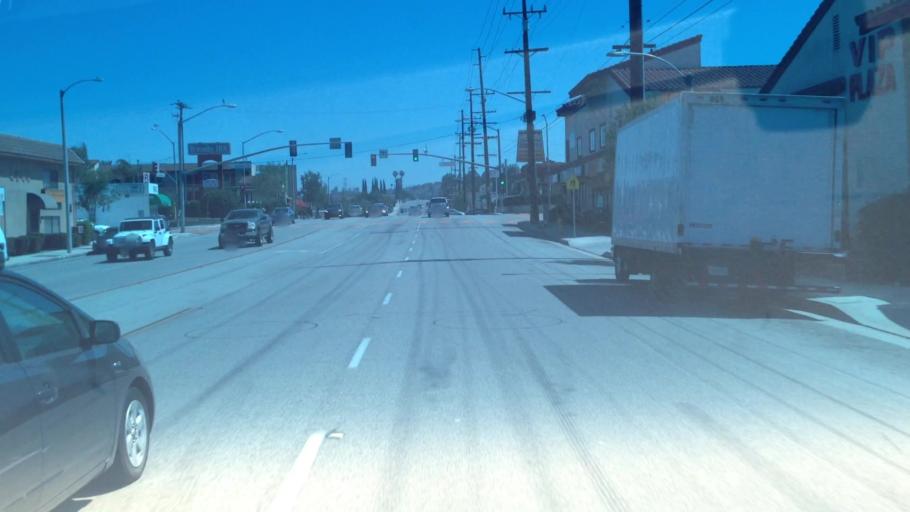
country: US
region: California
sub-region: Los Angeles County
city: South San Gabriel
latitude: 34.0547
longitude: -118.0907
